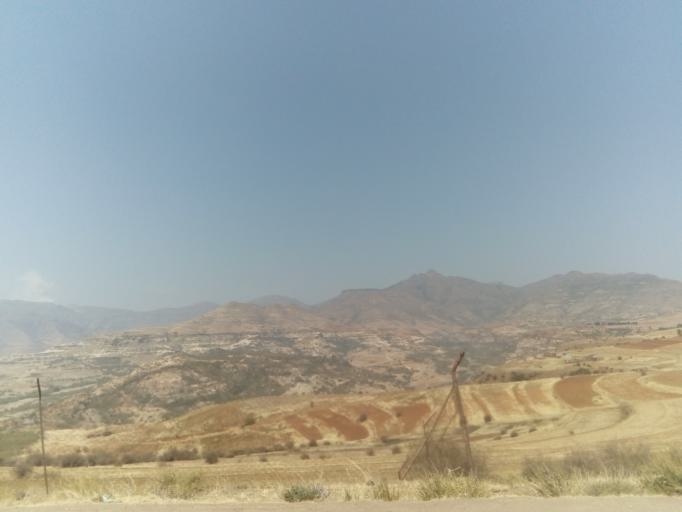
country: LS
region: Leribe
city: Leribe
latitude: -29.1491
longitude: 28.0470
